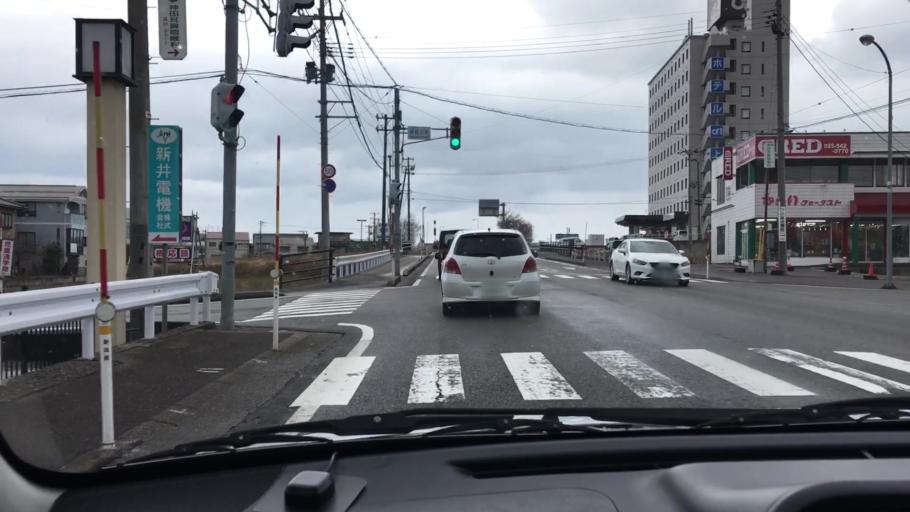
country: JP
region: Niigata
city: Joetsu
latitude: 37.1652
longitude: 138.2372
